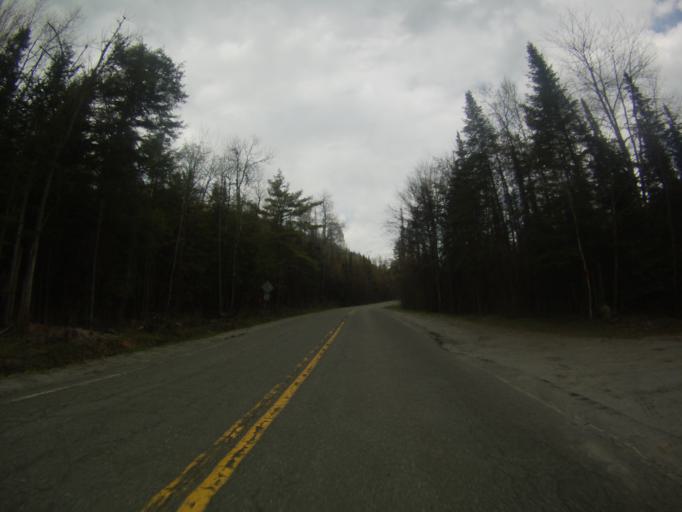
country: US
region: New York
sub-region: Essex County
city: Mineville
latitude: 44.0898
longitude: -73.5834
